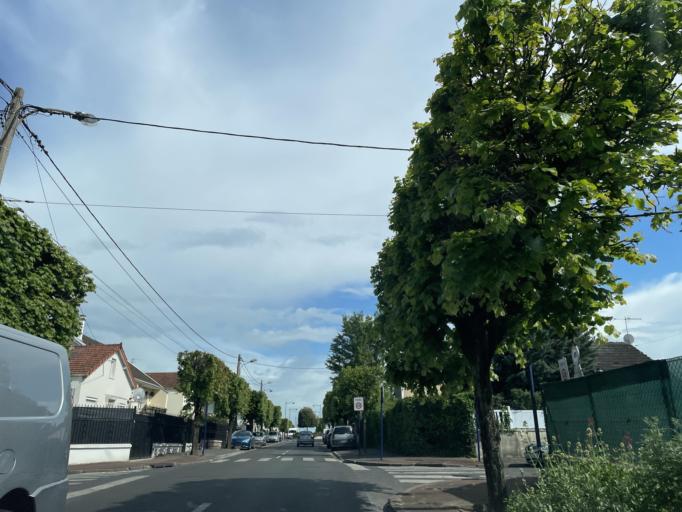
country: FR
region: Ile-de-France
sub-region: Departement du Val-d'Oise
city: Arnouville
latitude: 48.9843
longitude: 2.4175
